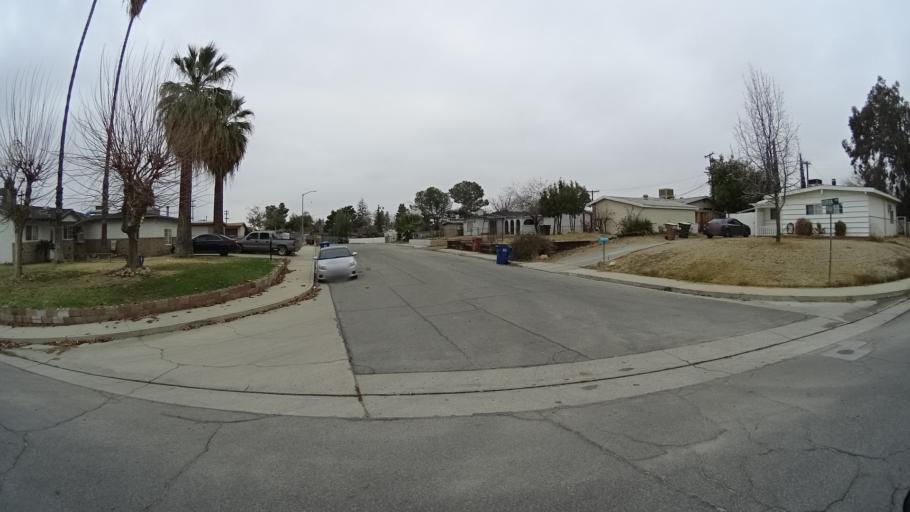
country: US
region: California
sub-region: Kern County
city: Bakersfield
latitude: 35.3816
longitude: -118.9296
